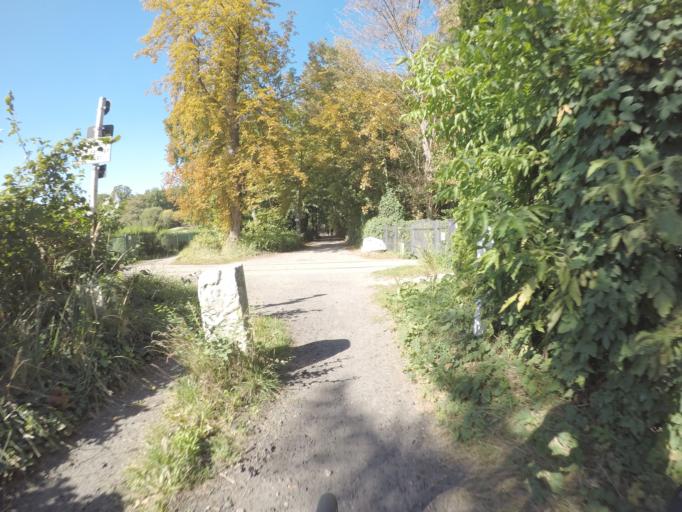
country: DE
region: Berlin
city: Heiligensee
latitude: 52.5930
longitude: 13.2652
